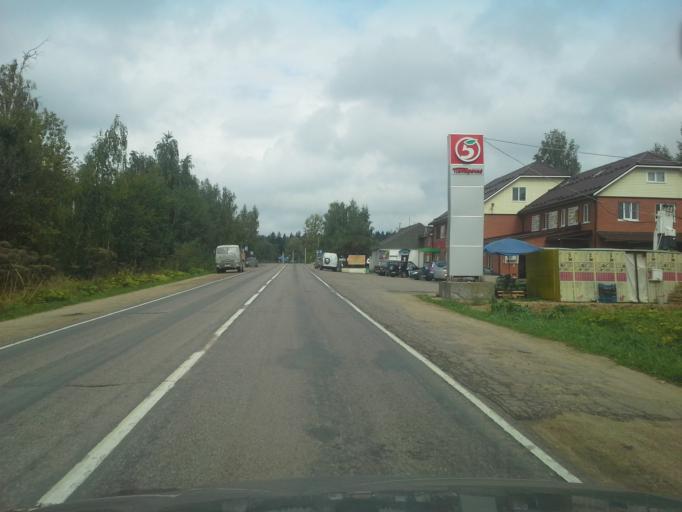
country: RU
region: Moskovskaya
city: Ruza
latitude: 55.7578
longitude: 36.1445
